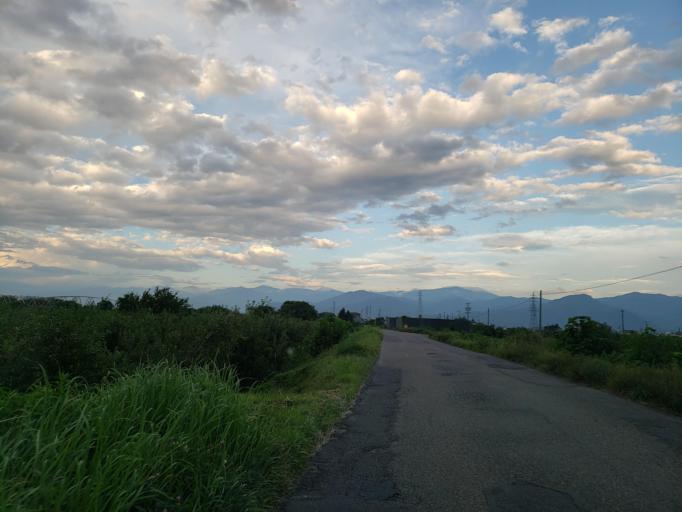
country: JP
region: Nagano
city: Nagano-shi
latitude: 36.6192
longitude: 138.1371
